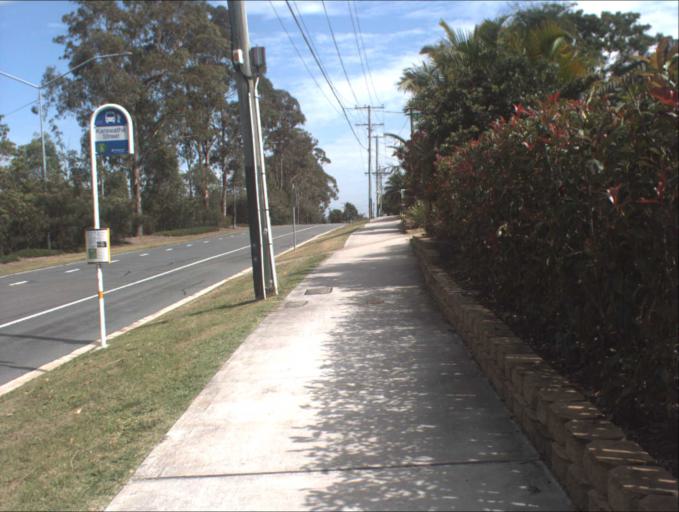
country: AU
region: Queensland
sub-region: Logan
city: Springwood
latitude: -27.6236
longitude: 153.1467
